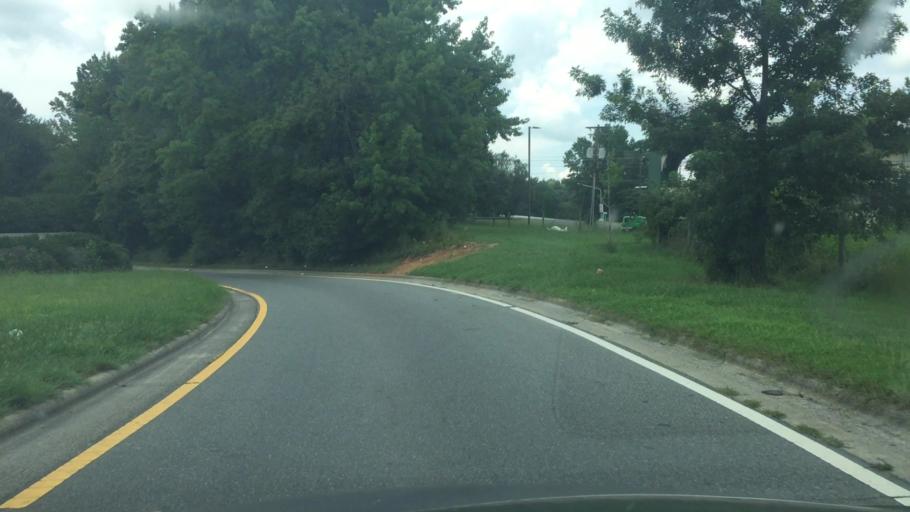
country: US
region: North Carolina
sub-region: Randolph County
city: Asheboro
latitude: 35.6869
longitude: -79.8289
